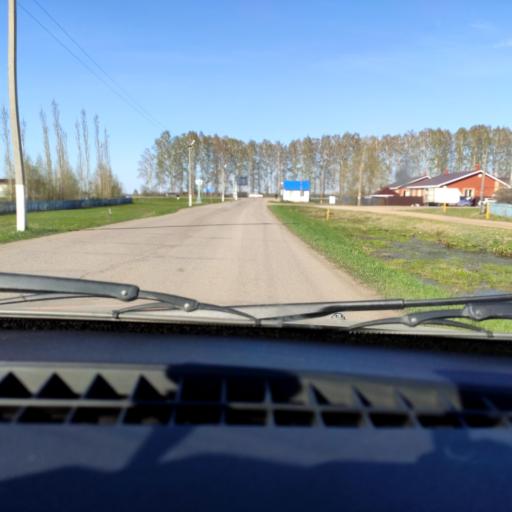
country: RU
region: Bashkortostan
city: Kabakovo
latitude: 54.6045
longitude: 56.1862
